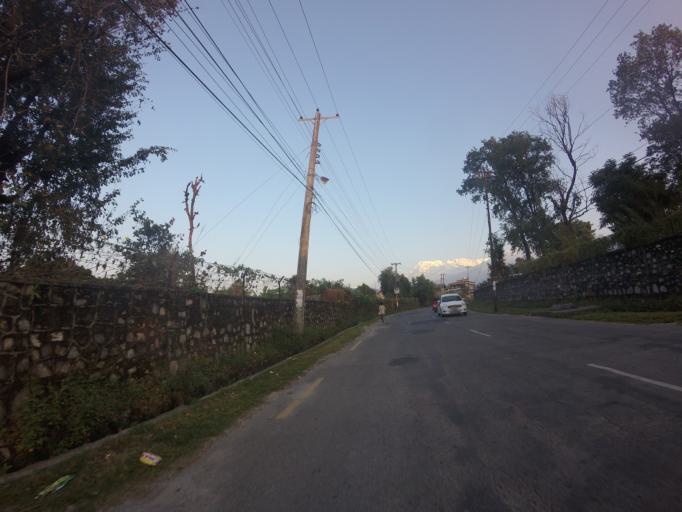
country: NP
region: Western Region
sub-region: Gandaki Zone
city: Pokhara
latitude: 28.2136
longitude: 83.9984
